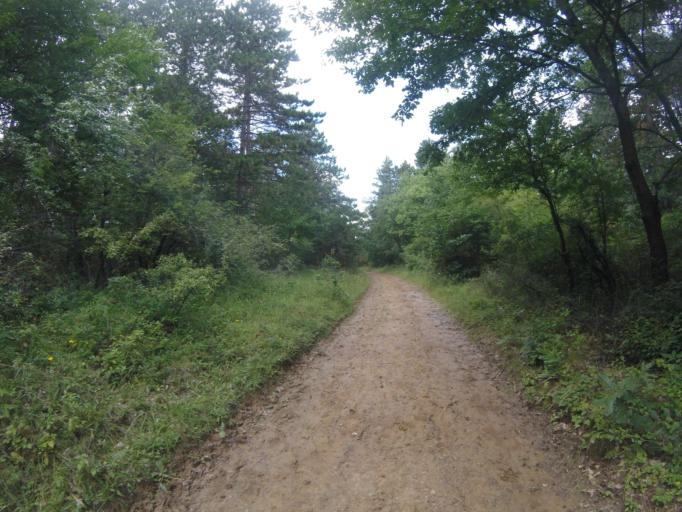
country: SK
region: Nitriansky
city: Sahy
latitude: 48.0227
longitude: 18.9504
